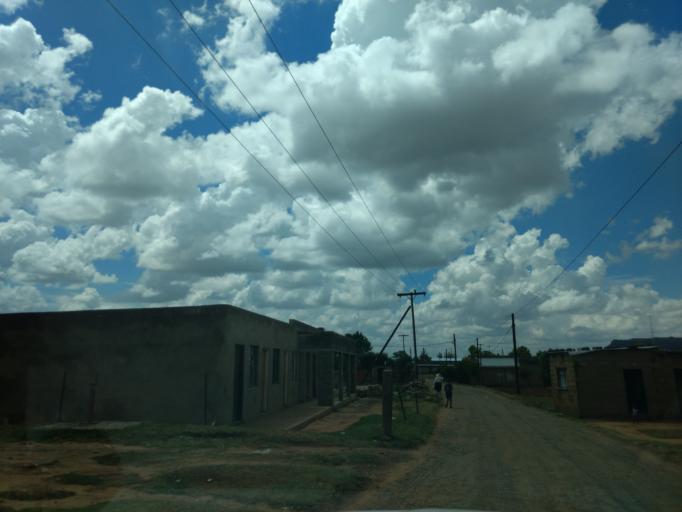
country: LS
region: Maseru
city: Maseru
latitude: -29.3714
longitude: 27.5113
